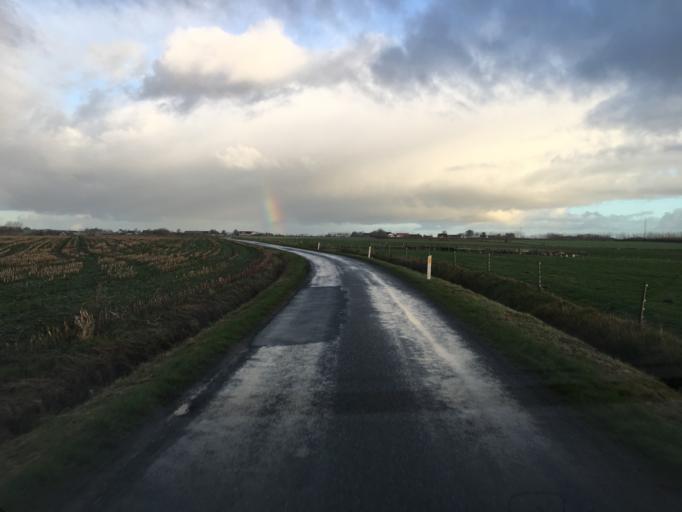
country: DK
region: South Denmark
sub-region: Tonder Kommune
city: Sherrebek
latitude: 55.1465
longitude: 8.8264
